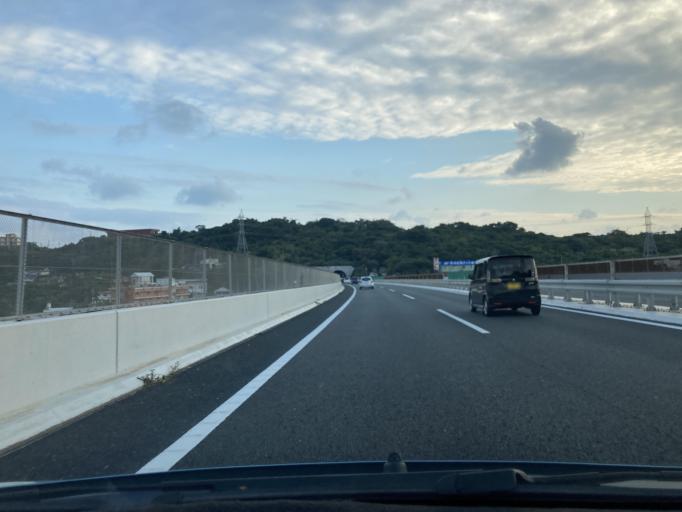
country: JP
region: Okinawa
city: Chatan
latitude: 26.3116
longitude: 127.7880
